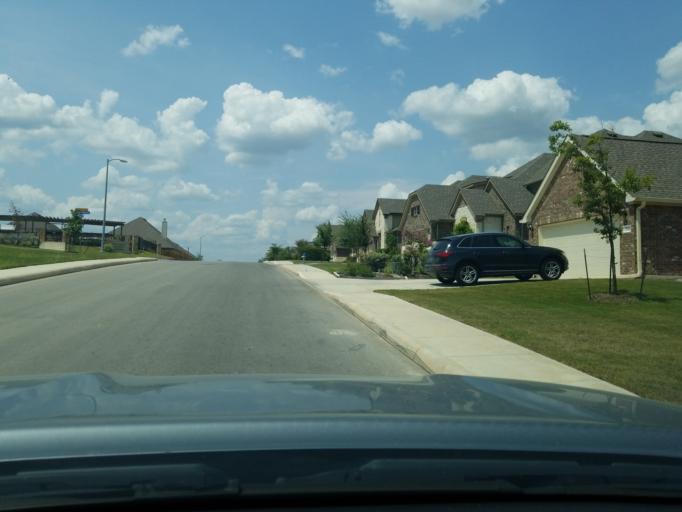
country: US
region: Texas
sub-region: Bexar County
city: Timberwood Park
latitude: 29.6821
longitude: -98.4787
